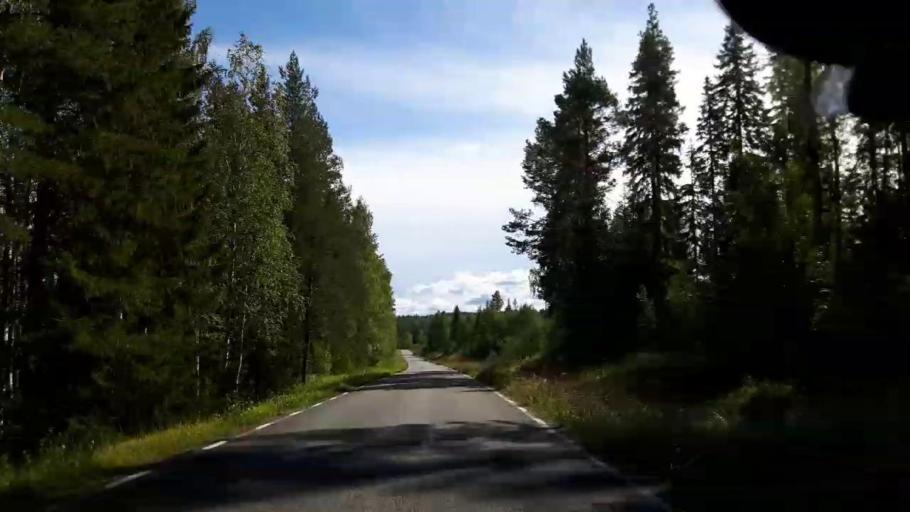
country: SE
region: Jaemtland
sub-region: OEstersunds Kommun
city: Lit
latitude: 63.2297
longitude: 15.2668
